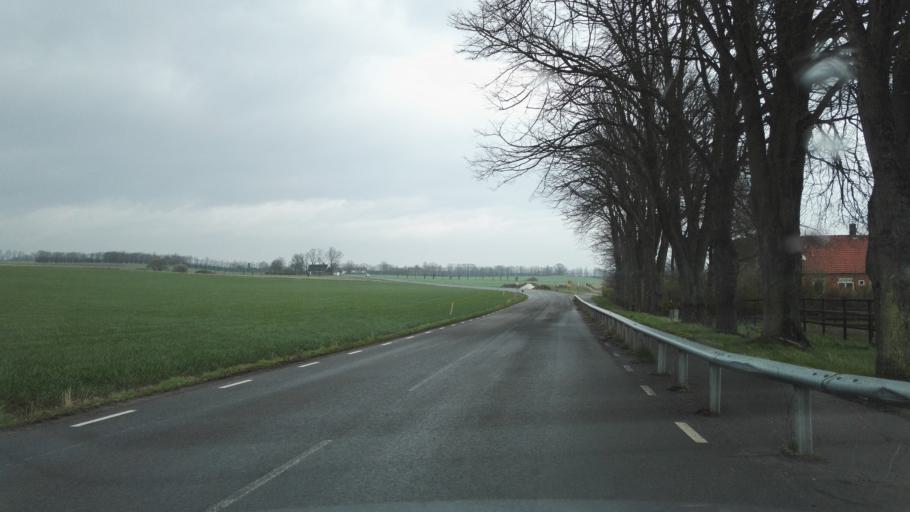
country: SE
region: Skane
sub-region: Simrishamns Kommun
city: Simrishamn
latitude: 55.4838
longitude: 14.2848
